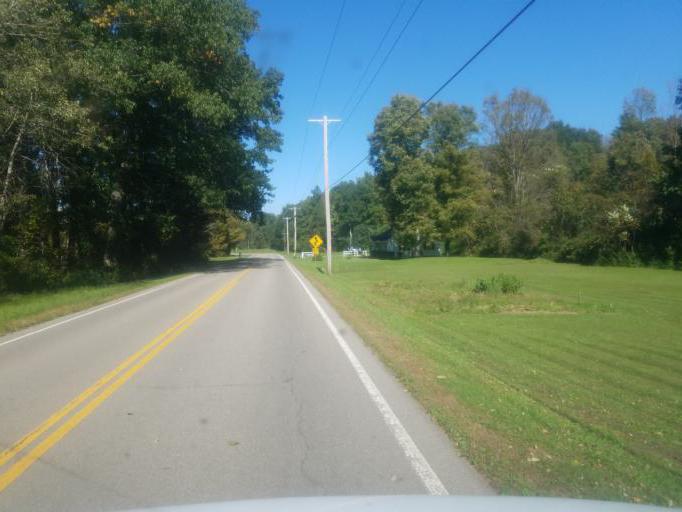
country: US
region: New York
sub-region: Allegany County
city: Friendship
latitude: 42.3093
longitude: -78.1079
